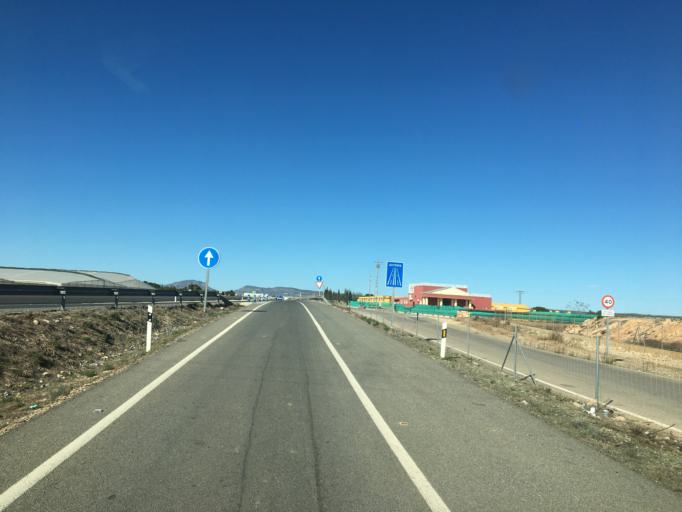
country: ES
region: Murcia
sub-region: Murcia
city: San Javier
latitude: 37.8531
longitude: -0.8810
